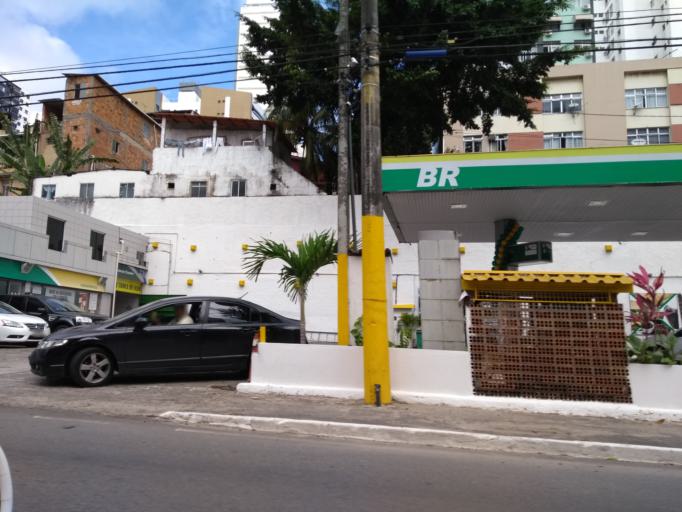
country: BR
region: Bahia
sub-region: Salvador
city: Salvador
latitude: -12.9913
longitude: -38.5235
